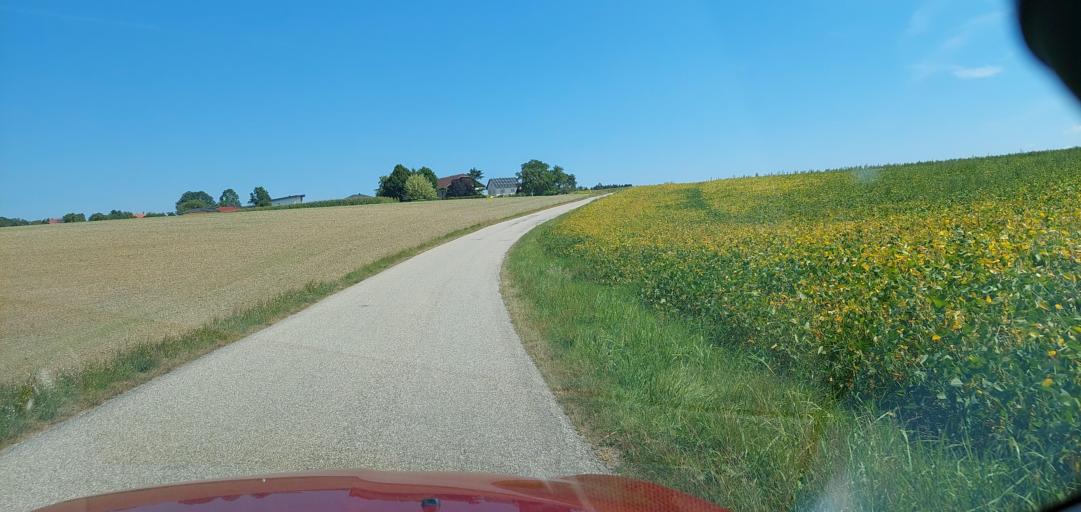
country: AT
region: Upper Austria
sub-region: Wels-Land
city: Offenhausen
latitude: 48.1378
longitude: 13.8300
